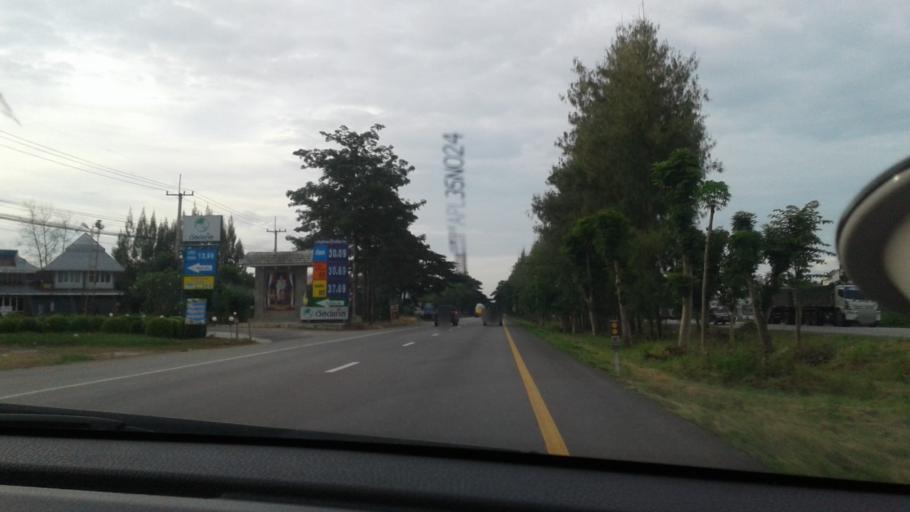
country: TH
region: Prachuap Khiri Khan
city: Pran Buri
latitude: 12.4352
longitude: 99.9128
